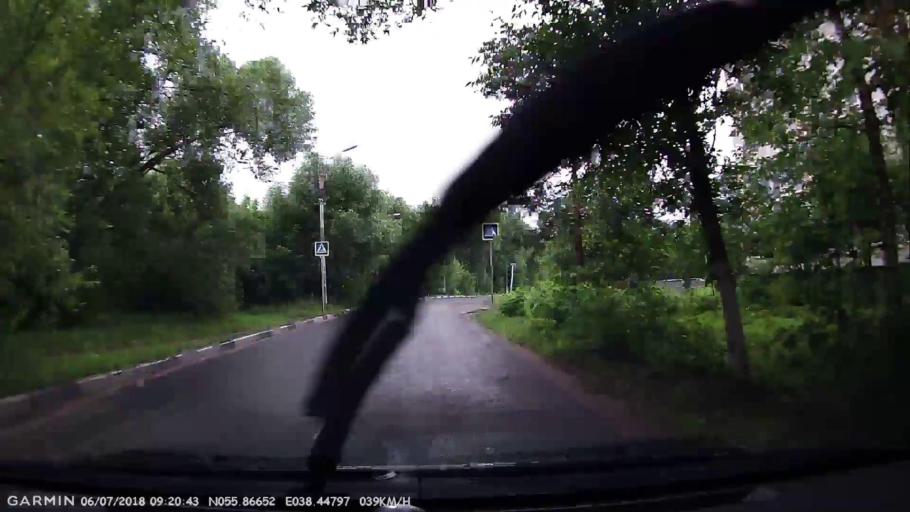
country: RU
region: Moskovskaya
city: Noginsk
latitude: 55.8664
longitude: 38.4481
